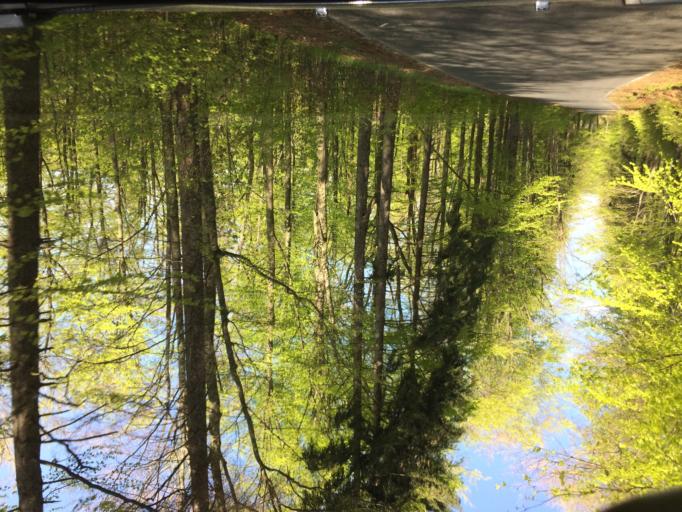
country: PL
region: Lower Silesian Voivodeship
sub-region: Powiat klodzki
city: Jugow
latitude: 50.6668
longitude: 16.5270
